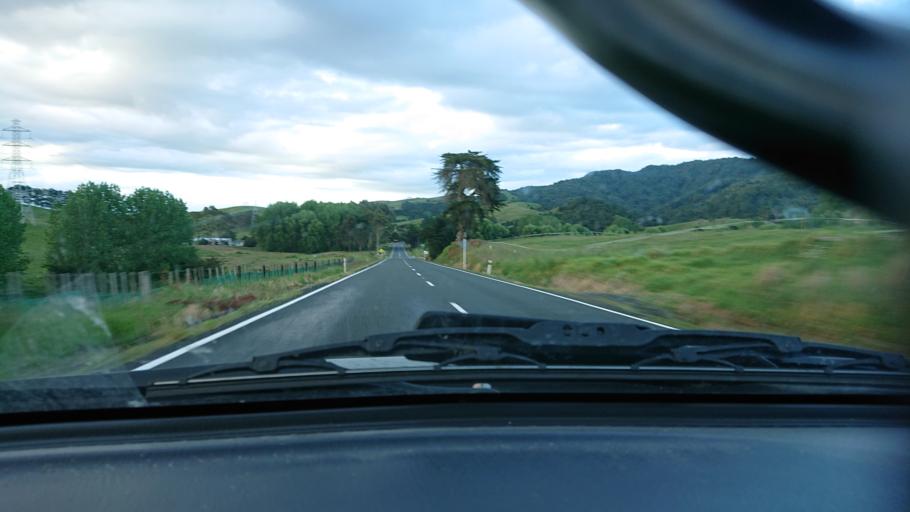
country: NZ
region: Auckland
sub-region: Auckland
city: Parakai
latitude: -36.4669
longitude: 174.4463
